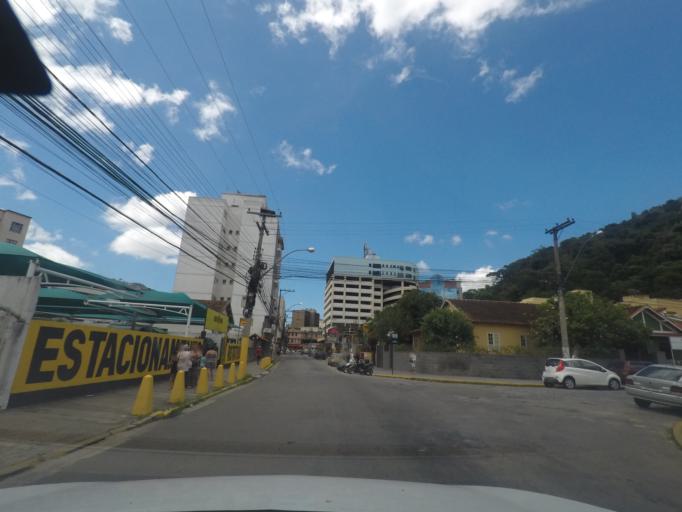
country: BR
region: Rio de Janeiro
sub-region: Teresopolis
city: Teresopolis
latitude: -22.4088
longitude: -42.9678
